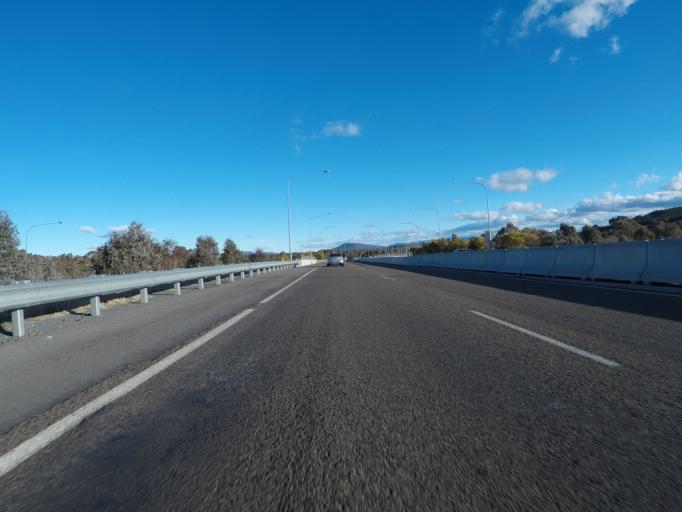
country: AU
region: Australian Capital Territory
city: Acton
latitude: -35.2801
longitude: 149.0865
